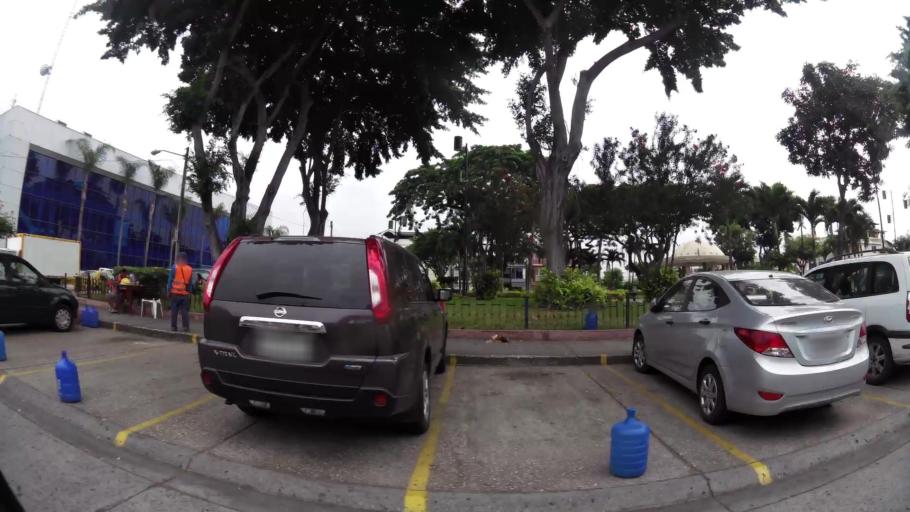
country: EC
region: Guayas
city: Eloy Alfaro
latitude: -2.1459
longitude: -79.8926
